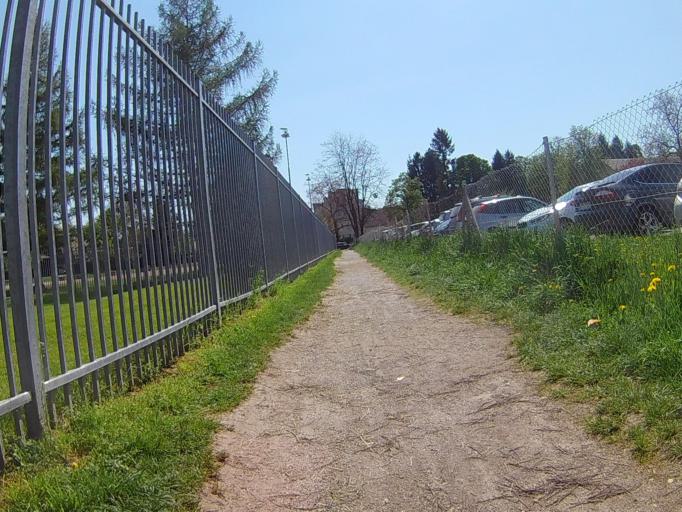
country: SI
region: Maribor
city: Maribor
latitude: 46.5467
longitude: 15.6327
